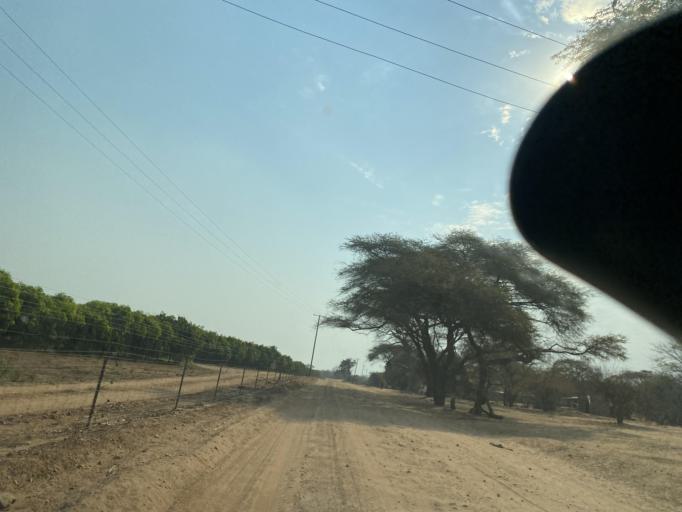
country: ZW
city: Chirundu
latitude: -15.9334
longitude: 28.9461
